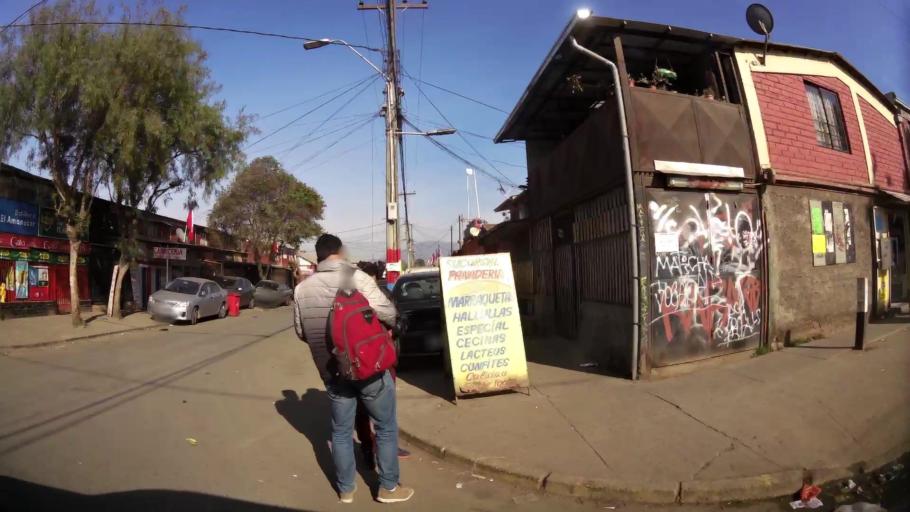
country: CL
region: Santiago Metropolitan
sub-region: Provincia de Santiago
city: Lo Prado
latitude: -33.4181
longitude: -70.7652
